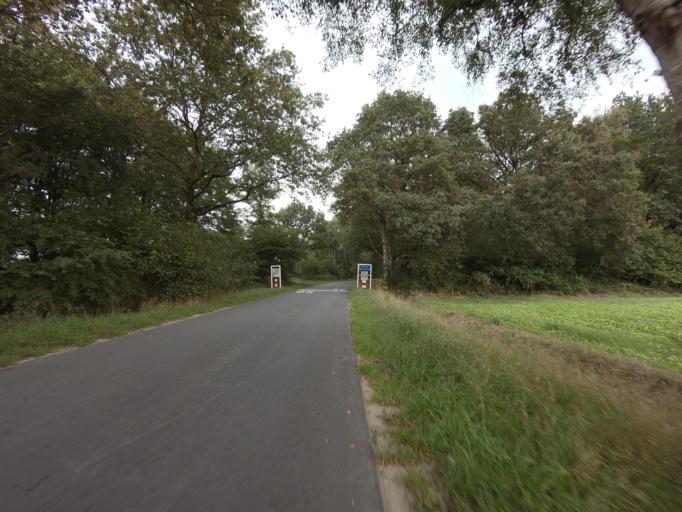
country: NL
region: Drenthe
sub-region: Gemeente Tynaarlo
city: Vries
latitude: 53.0657
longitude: 6.5816
